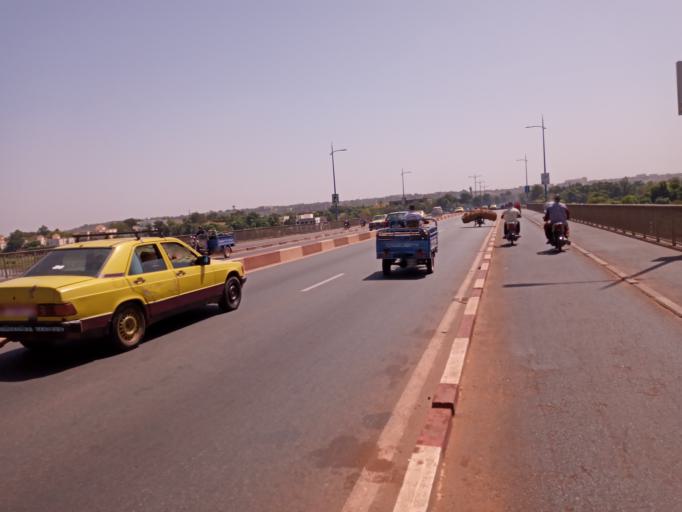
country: ML
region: Bamako
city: Bamako
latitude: 12.6218
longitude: -8.0035
